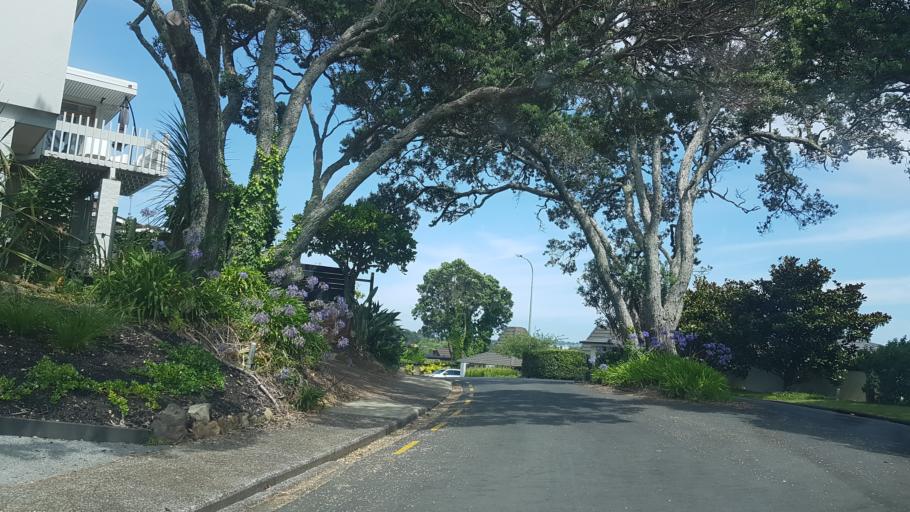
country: NZ
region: Auckland
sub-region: Auckland
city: North Shore
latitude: -36.7838
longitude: 174.7703
